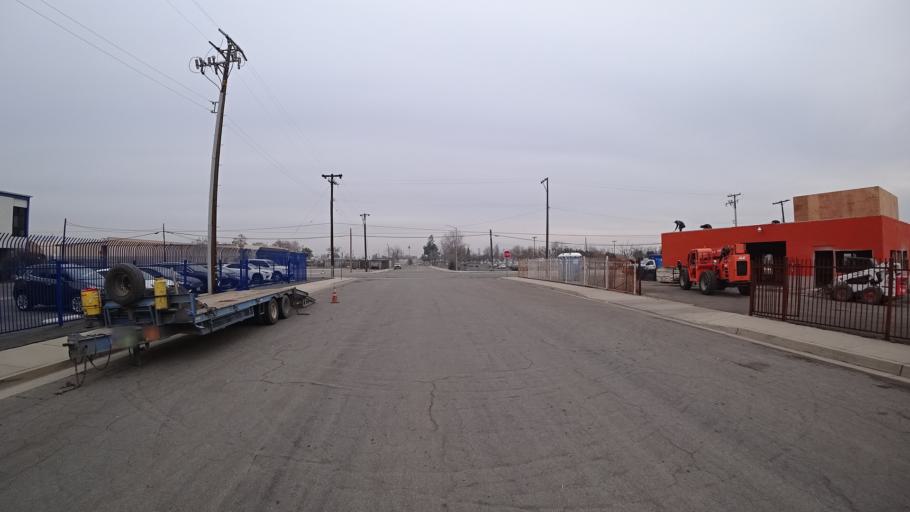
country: US
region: California
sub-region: Kern County
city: Bakersfield
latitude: 35.3711
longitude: -119.0023
